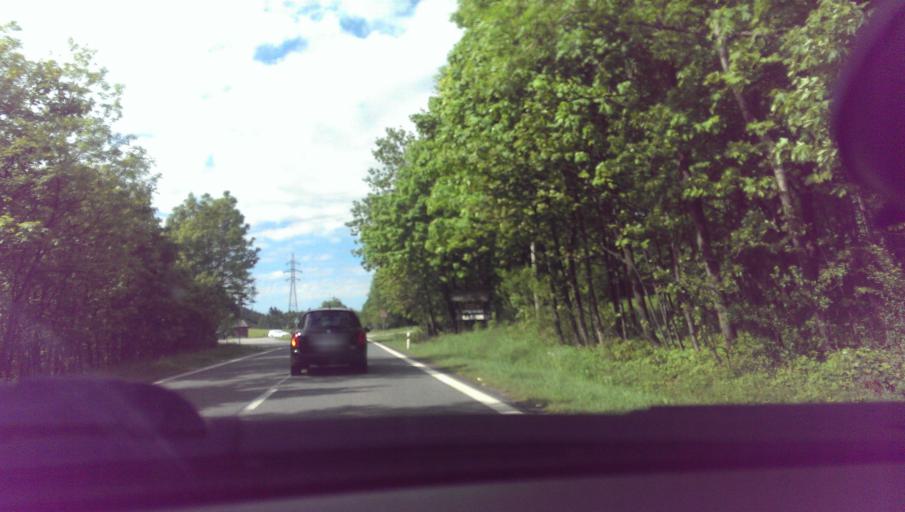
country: CZ
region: Zlin
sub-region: Okres Vsetin
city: Dolni Becva
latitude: 49.5017
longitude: 18.1878
